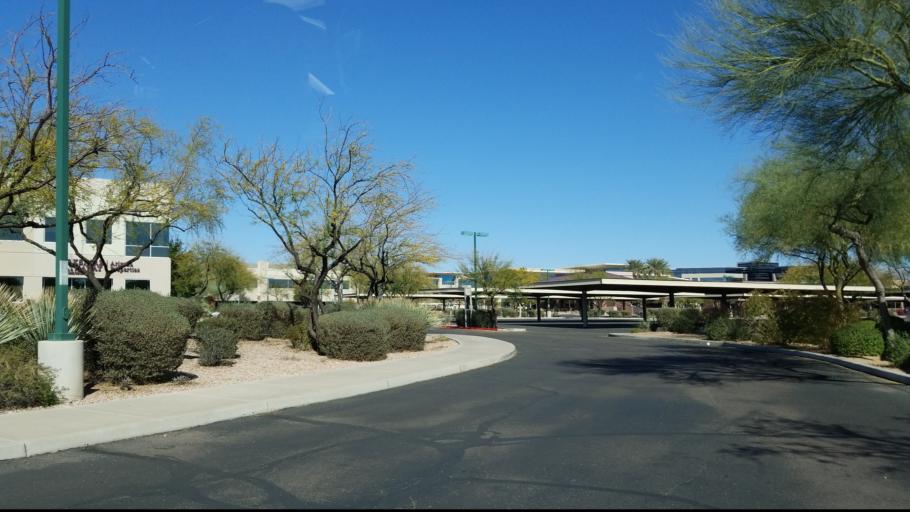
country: US
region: Arizona
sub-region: Maricopa County
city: Paradise Valley
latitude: 33.6193
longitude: -111.9304
